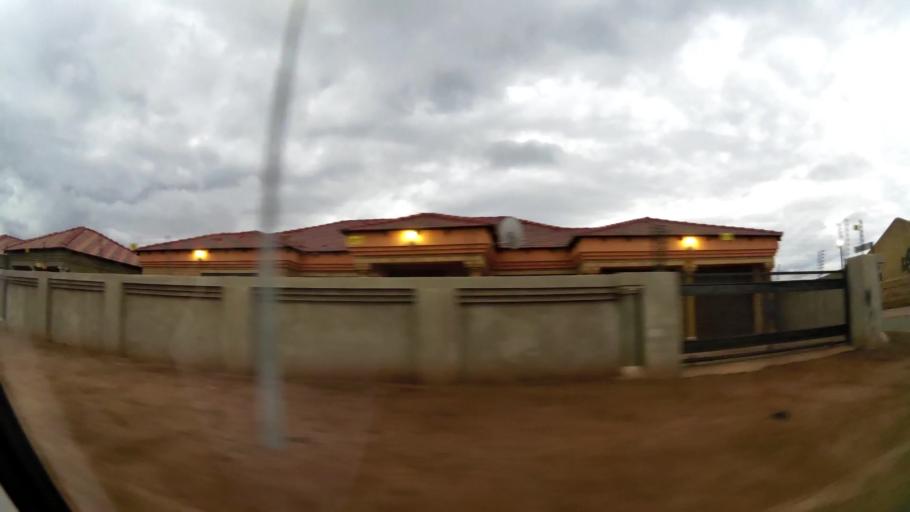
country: ZA
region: Limpopo
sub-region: Waterberg District Municipality
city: Mokopane
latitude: -24.1993
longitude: 28.9951
